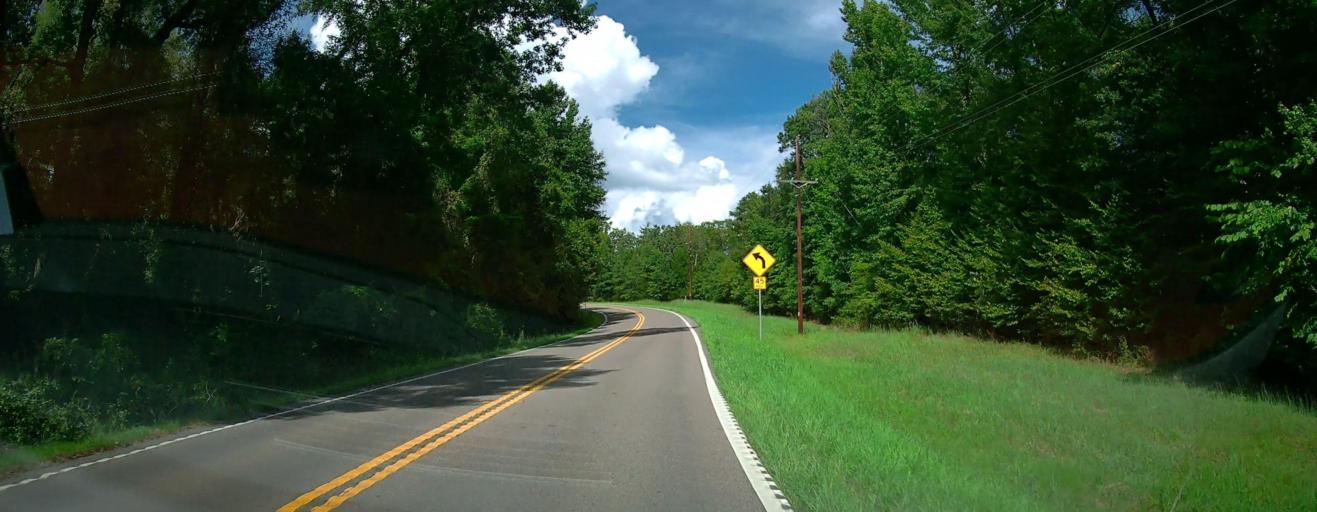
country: US
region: Georgia
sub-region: Talbot County
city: Talbotton
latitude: 32.6227
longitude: -84.4882
